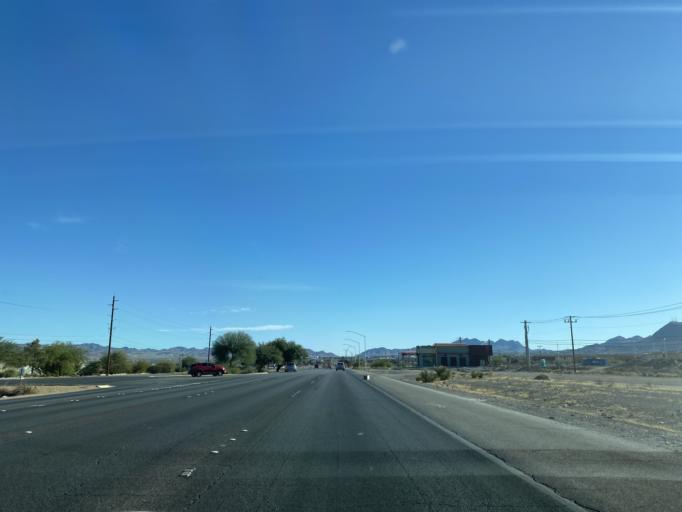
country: US
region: Nevada
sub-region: Clark County
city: Henderson
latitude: 36.0732
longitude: -115.0200
